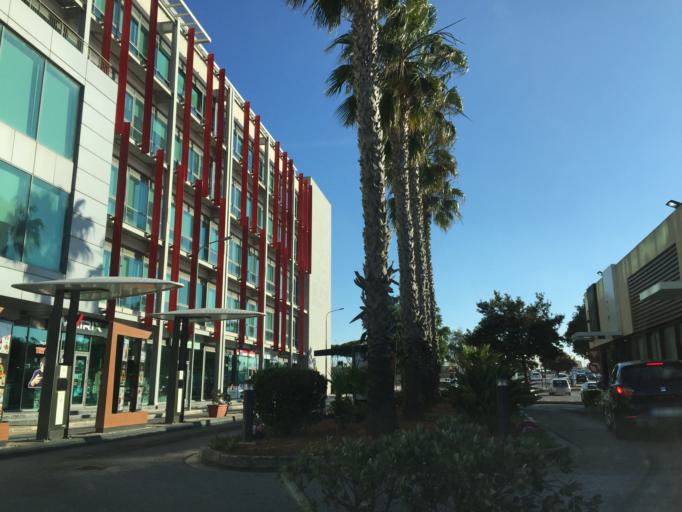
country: MT
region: Il-Gudja
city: Gudja
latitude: 35.8515
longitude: 14.4946
